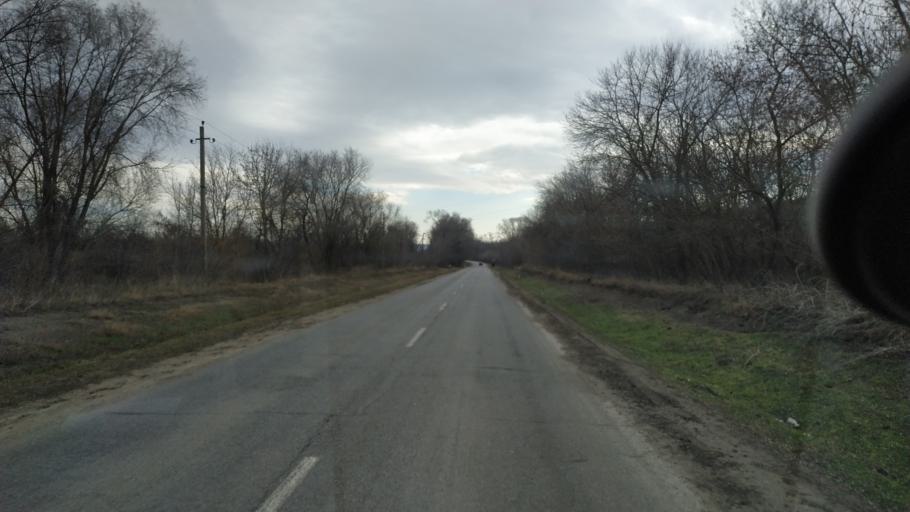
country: MD
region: Chisinau
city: Vadul lui Voda
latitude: 47.1330
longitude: 29.0618
